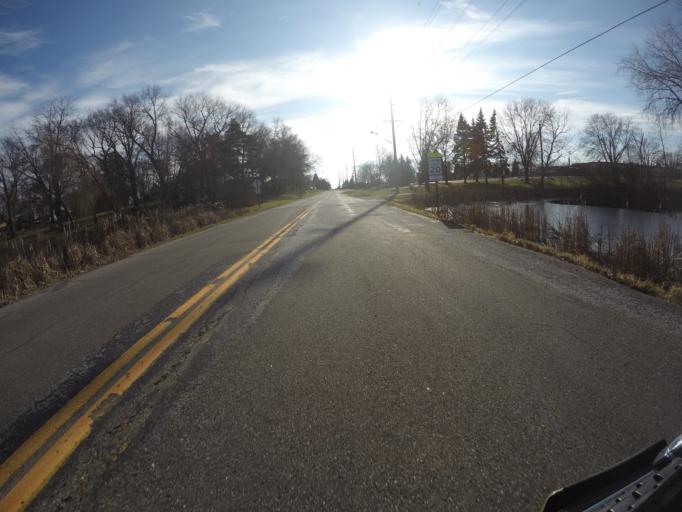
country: US
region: Minnesota
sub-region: Hennepin County
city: Eden Prairie
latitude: 44.8773
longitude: -93.4957
